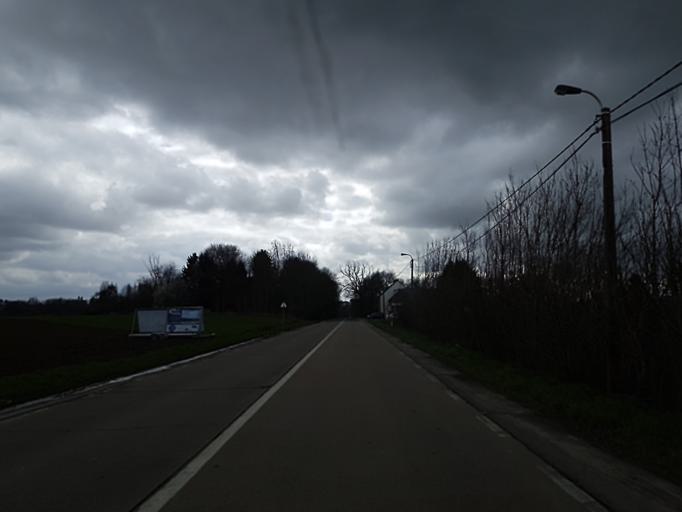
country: BE
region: Wallonia
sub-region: Province du Brabant Wallon
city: Jodoigne
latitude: 50.6985
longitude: 4.8480
